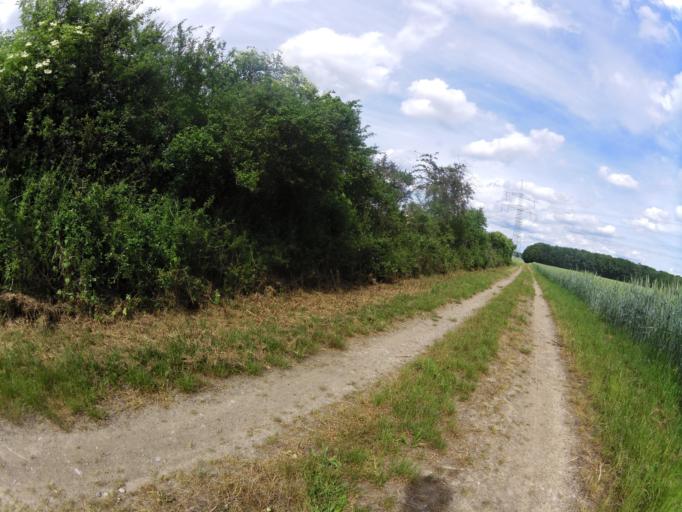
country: DE
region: Bavaria
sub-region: Regierungsbezirk Unterfranken
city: Ochsenfurt
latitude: 49.6966
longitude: 10.0647
